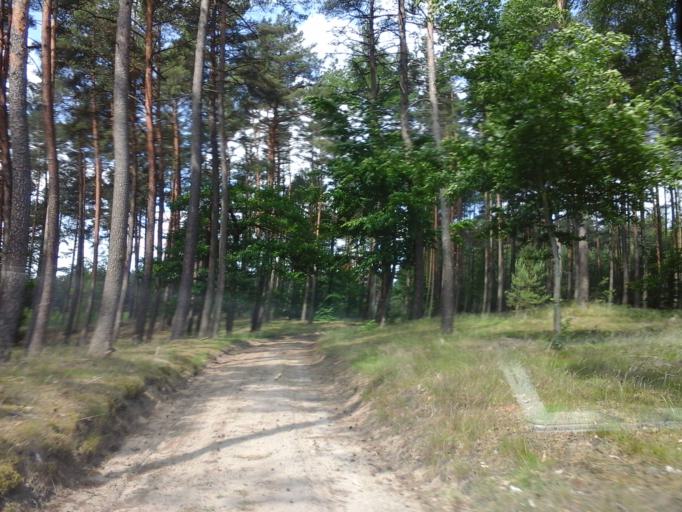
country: PL
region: West Pomeranian Voivodeship
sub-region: Powiat choszczenski
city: Bierzwnik
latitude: 53.0924
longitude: 15.7397
